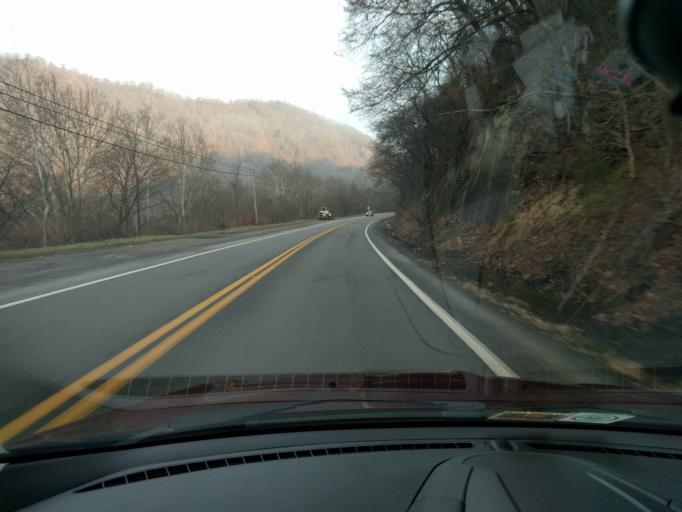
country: US
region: West Virginia
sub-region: Kanawha County
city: Montgomery
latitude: 38.1620
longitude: -81.3004
